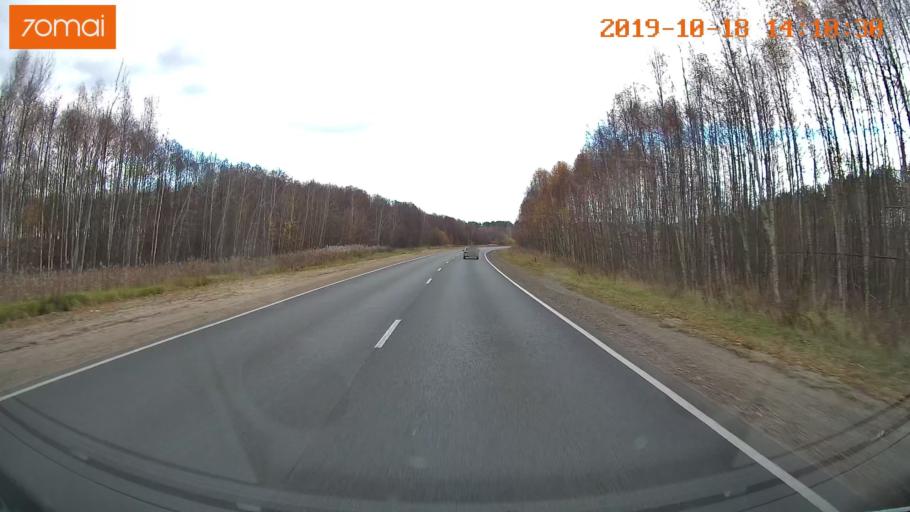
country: RU
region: Rjazan
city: Spas-Klepiki
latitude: 55.1417
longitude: 40.2093
